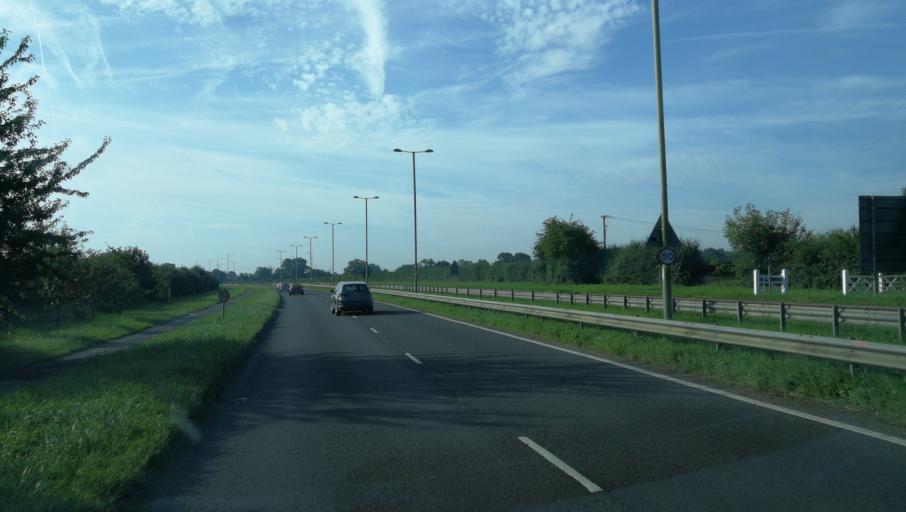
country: GB
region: England
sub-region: Oxfordshire
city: Yarnton
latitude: 51.8199
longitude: -1.3179
